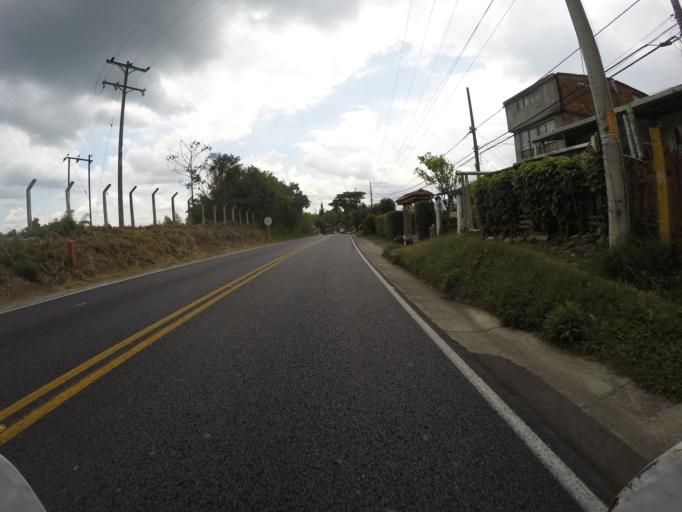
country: CO
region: Risaralda
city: Pereira
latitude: 4.7662
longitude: -75.6894
